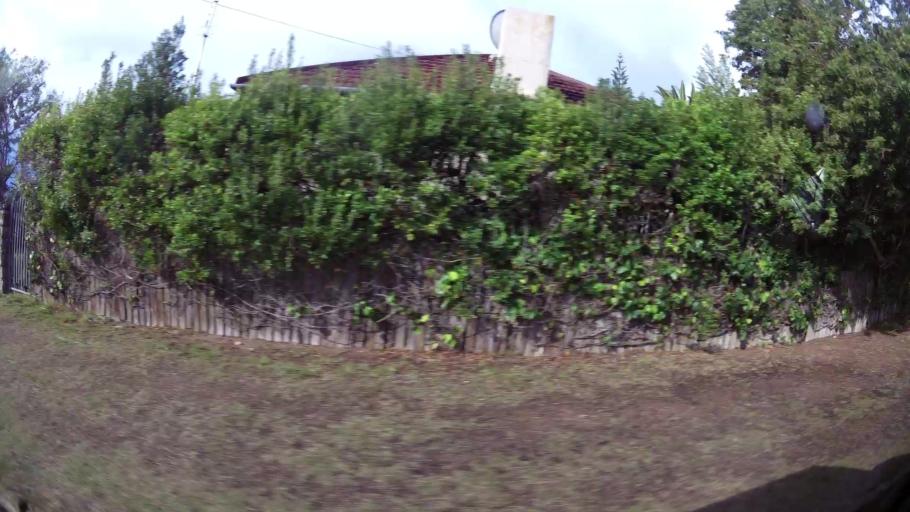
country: ZA
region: Western Cape
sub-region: Eden District Municipality
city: Mossel Bay
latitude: -34.1879
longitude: 22.1399
